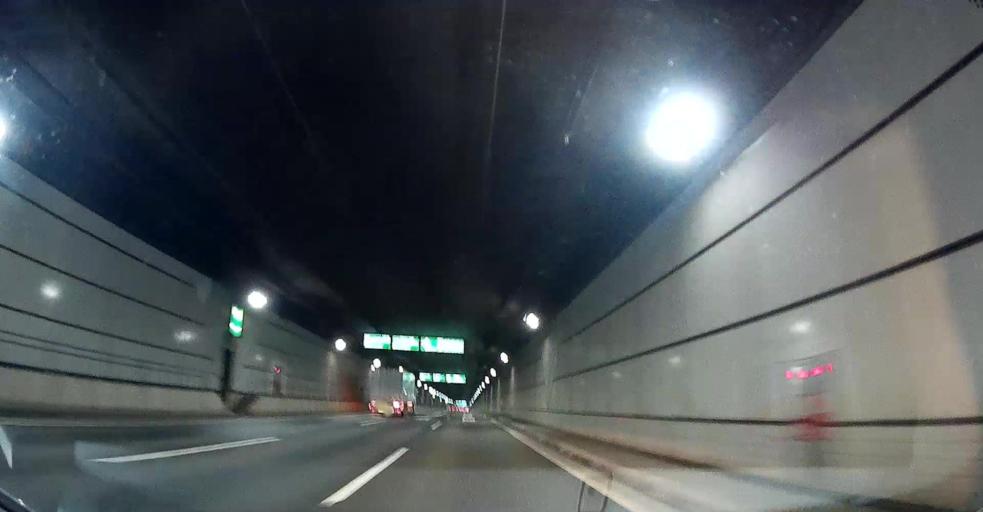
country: JP
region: Kanagawa
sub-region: Kawasaki-shi
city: Kawasaki
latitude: 35.5299
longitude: 139.7940
